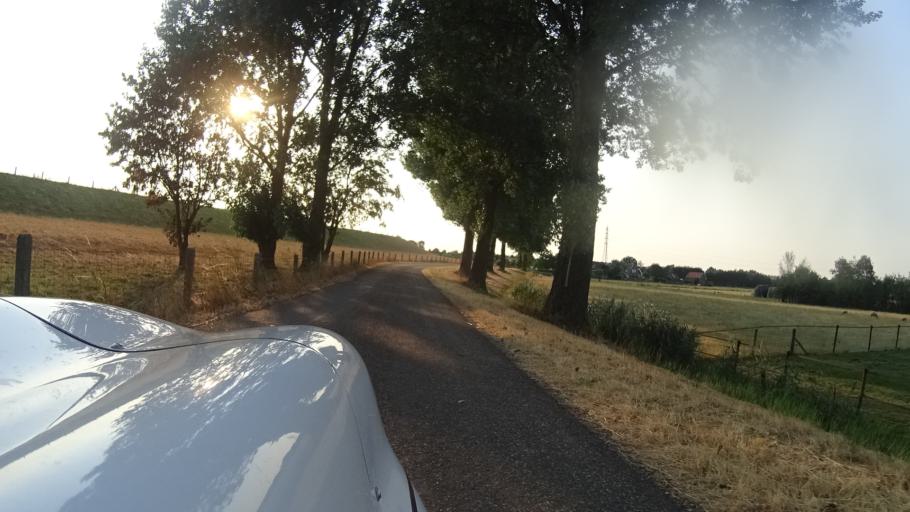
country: NL
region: Gelderland
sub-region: Gemeente Buren
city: Lienden
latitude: 51.9000
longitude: 5.4905
